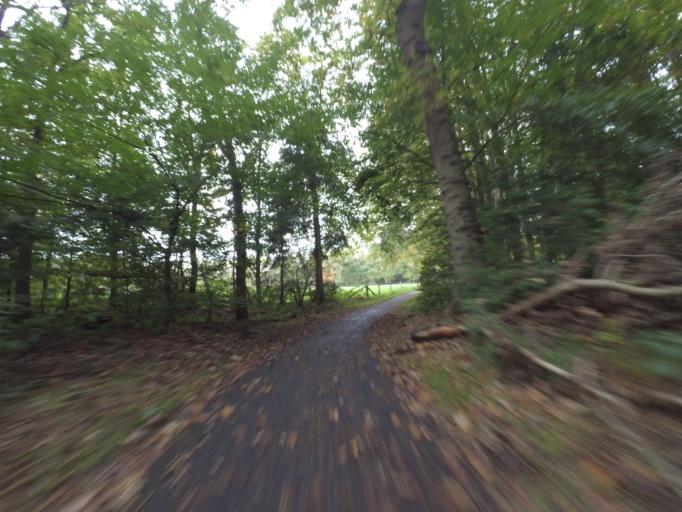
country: NL
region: Gelderland
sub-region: Gemeente Barneveld
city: Garderen
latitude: 52.3014
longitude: 5.7172
